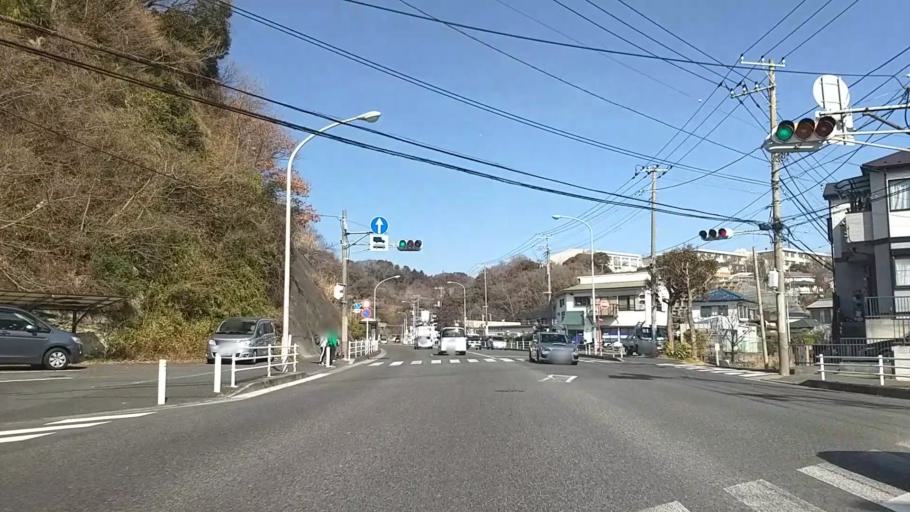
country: JP
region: Kanagawa
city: Zushi
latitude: 35.3484
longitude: 139.6081
